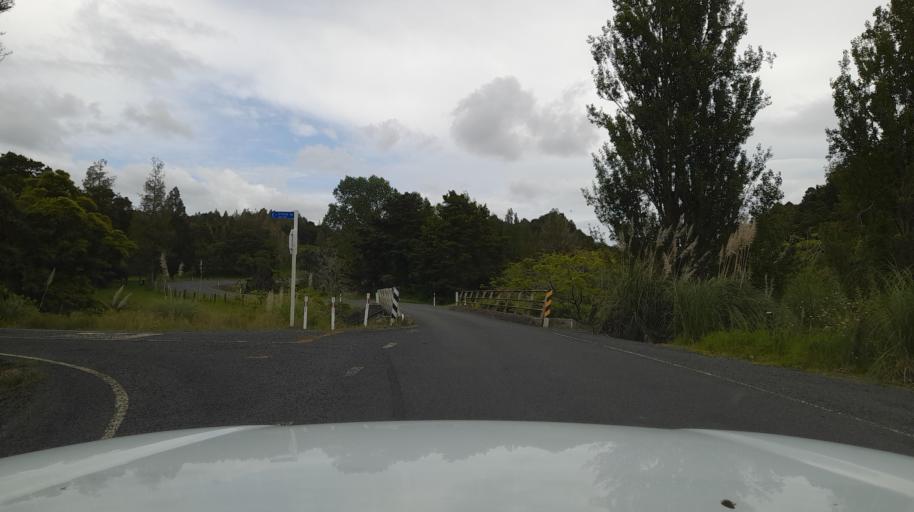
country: NZ
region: Northland
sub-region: Far North District
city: Kaitaia
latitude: -35.3036
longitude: 173.3532
